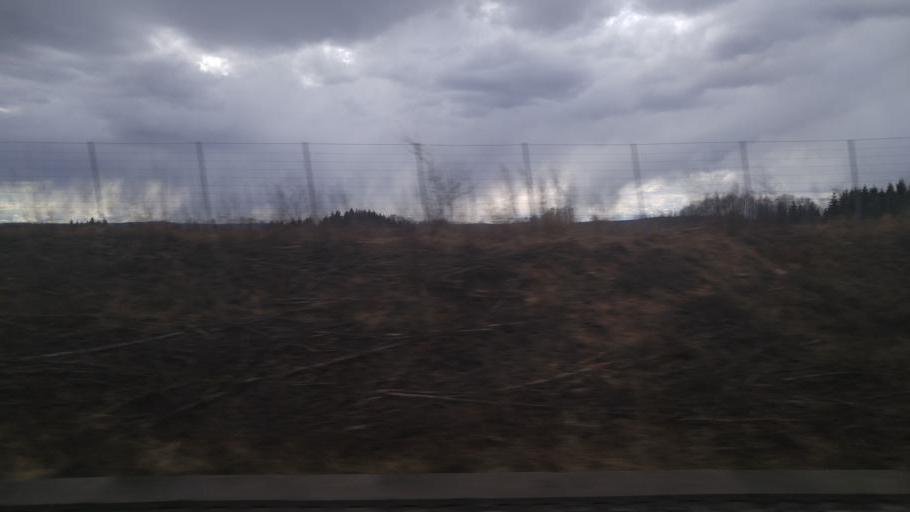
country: NO
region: Akershus
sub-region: Ullensaker
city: Jessheim
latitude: 60.1412
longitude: 11.1520
